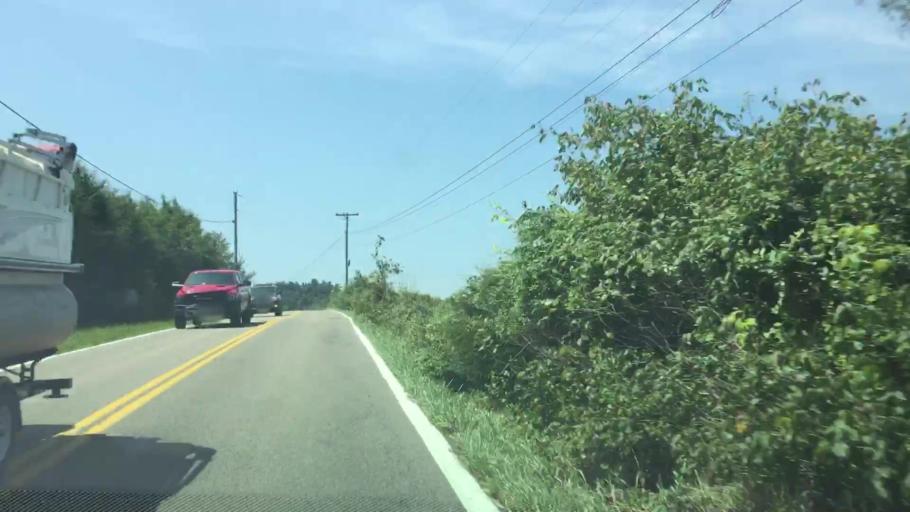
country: US
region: Tennessee
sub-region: Sullivan County
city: Fairmount
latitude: 36.5958
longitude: -82.0451
